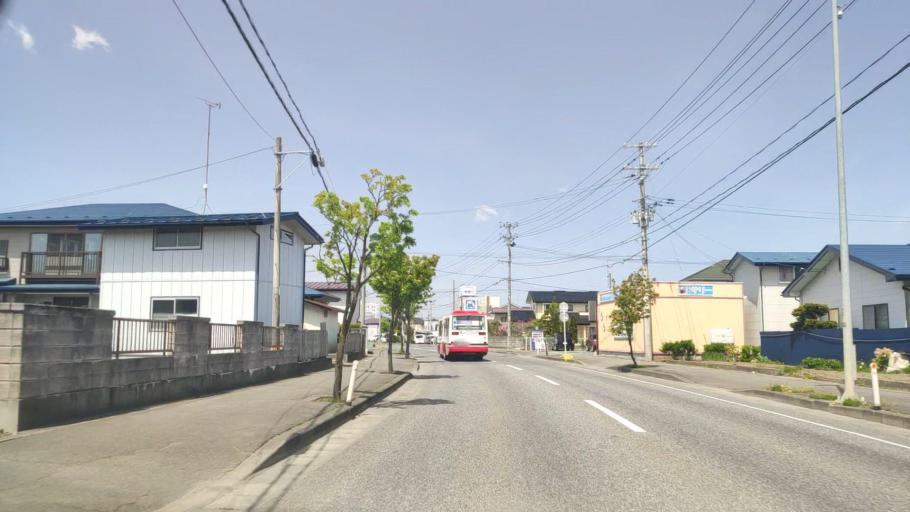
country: JP
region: Aomori
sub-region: Hachinohe Shi
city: Uchimaru
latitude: 40.5059
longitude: 141.4382
